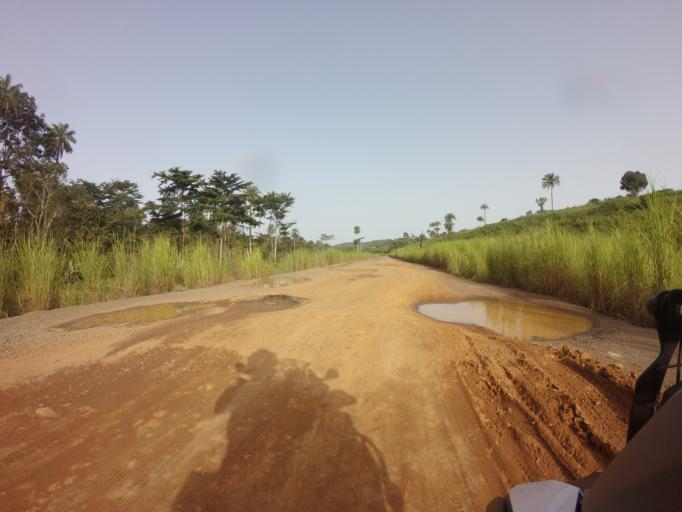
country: GN
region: Nzerekore
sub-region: Nzerekore Prefecture
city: Nzerekore
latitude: 8.0712
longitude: -9.0786
